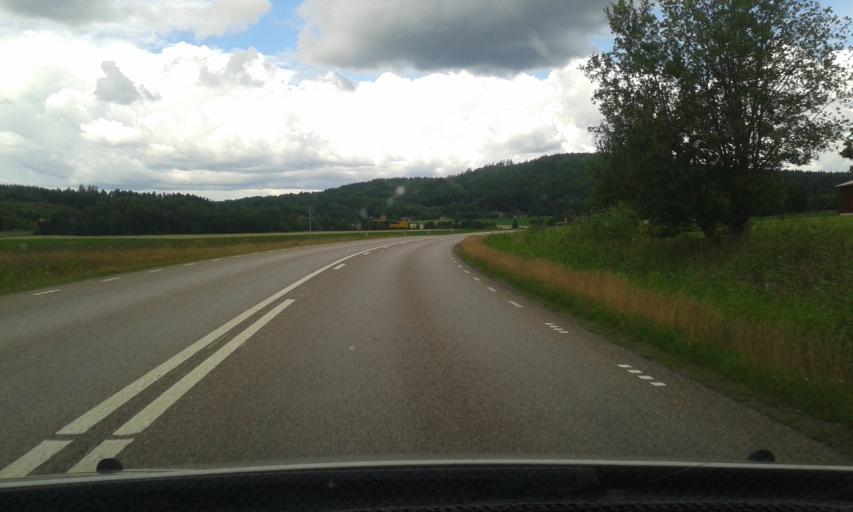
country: SE
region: Vaestra Goetaland
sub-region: Lilla Edets Kommun
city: Lilla Edet
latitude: 58.1363
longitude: 12.1008
